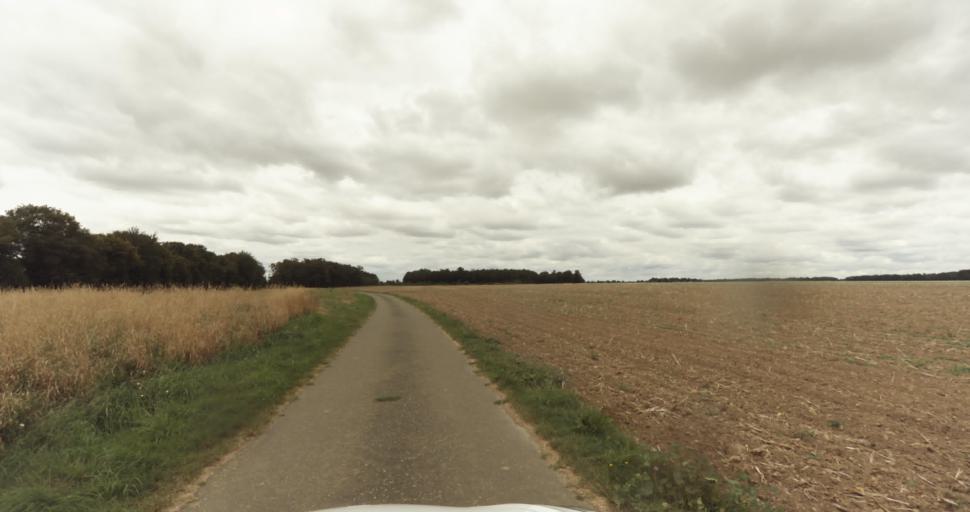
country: FR
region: Haute-Normandie
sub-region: Departement de l'Eure
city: Nonancourt
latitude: 48.8144
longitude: 1.1668
